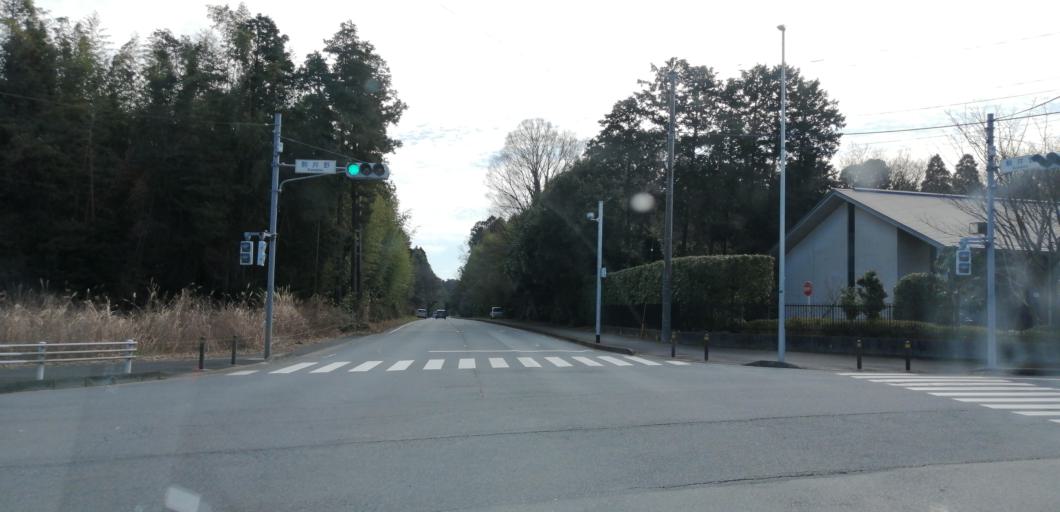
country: JP
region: Chiba
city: Narita
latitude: 35.7700
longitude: 140.3641
